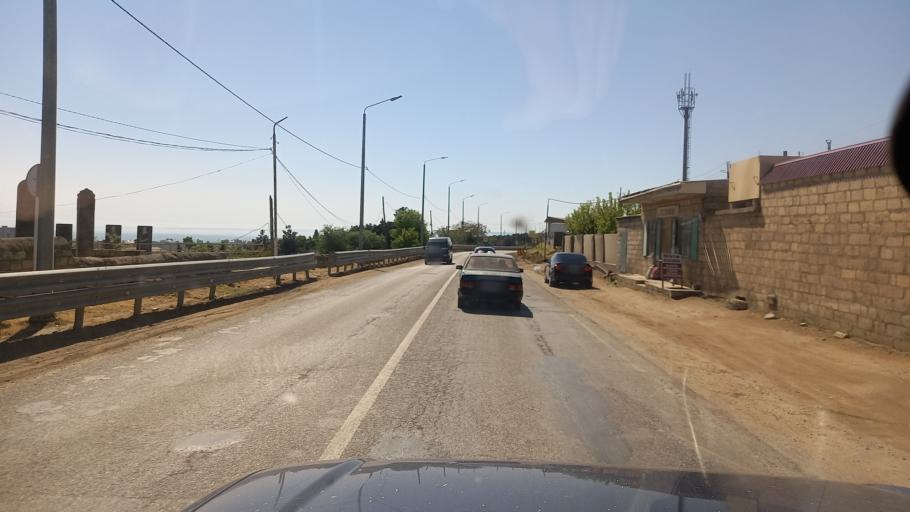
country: RU
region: Dagestan
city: Derbent
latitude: 42.0505
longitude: 48.2808
